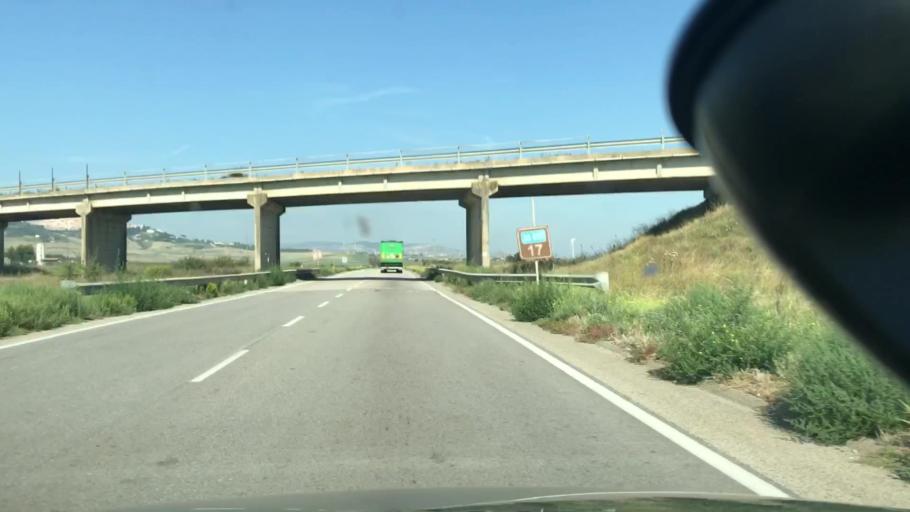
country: IT
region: Apulia
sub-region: Provincia di Foggia
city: Candela
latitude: 41.1237
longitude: 15.5665
